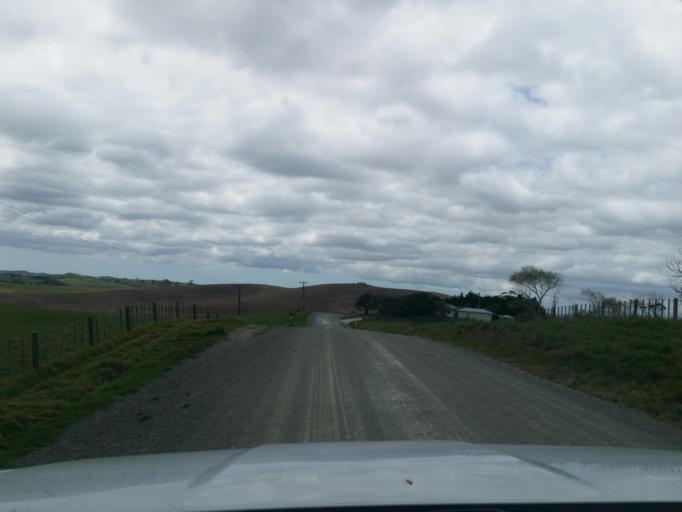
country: NZ
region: Auckland
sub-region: Auckland
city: Wellsford
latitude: -36.2874
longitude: 174.3394
